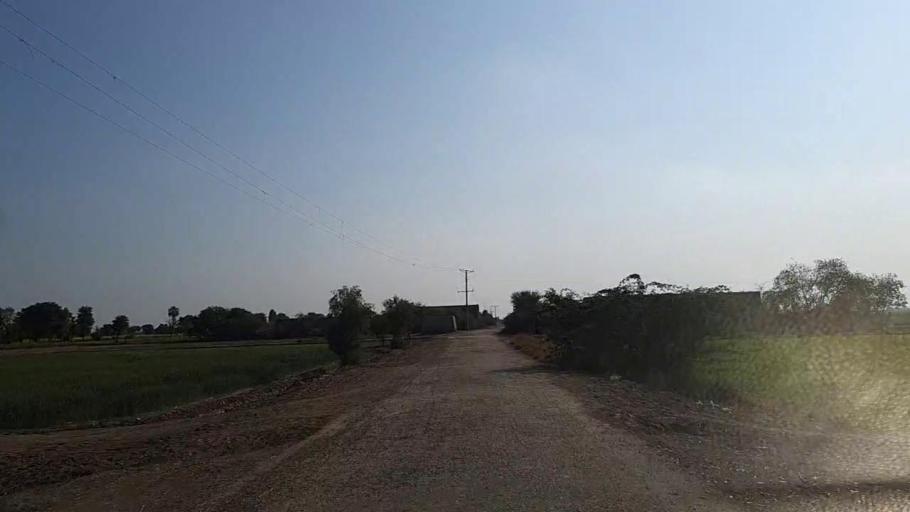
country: PK
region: Sindh
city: Jam Sahib
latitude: 26.2845
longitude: 68.6048
